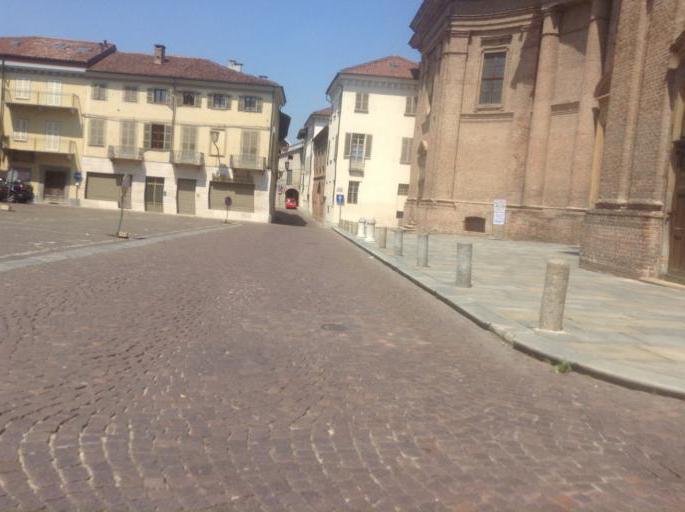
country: IT
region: Piedmont
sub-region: Provincia di Torino
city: Carignano
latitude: 44.9064
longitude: 7.6756
